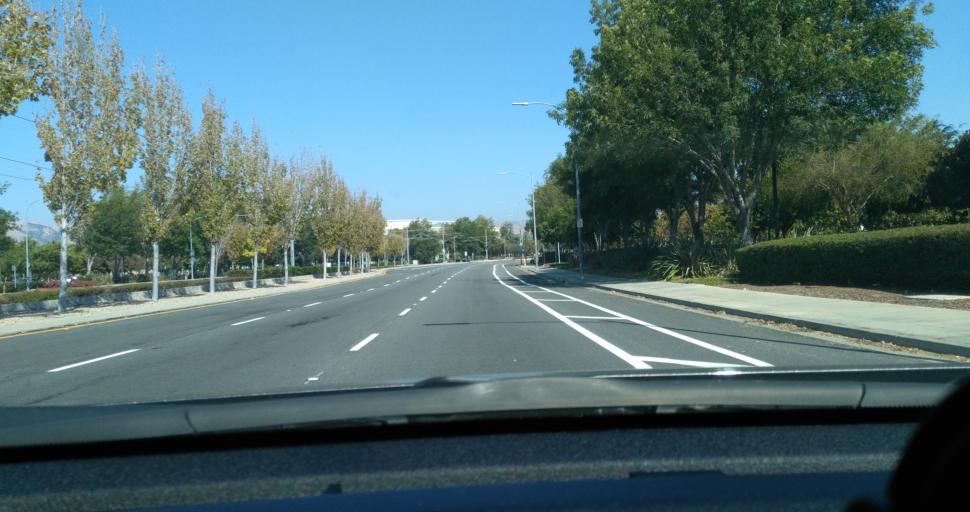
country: US
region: California
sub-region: Santa Clara County
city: Milpitas
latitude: 37.4129
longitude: -121.9347
